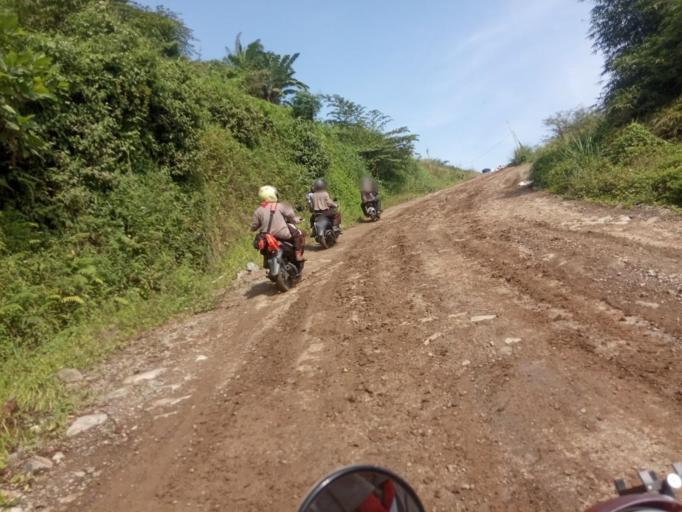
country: ID
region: West Java
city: Caringin
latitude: -6.6601
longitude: 106.8830
